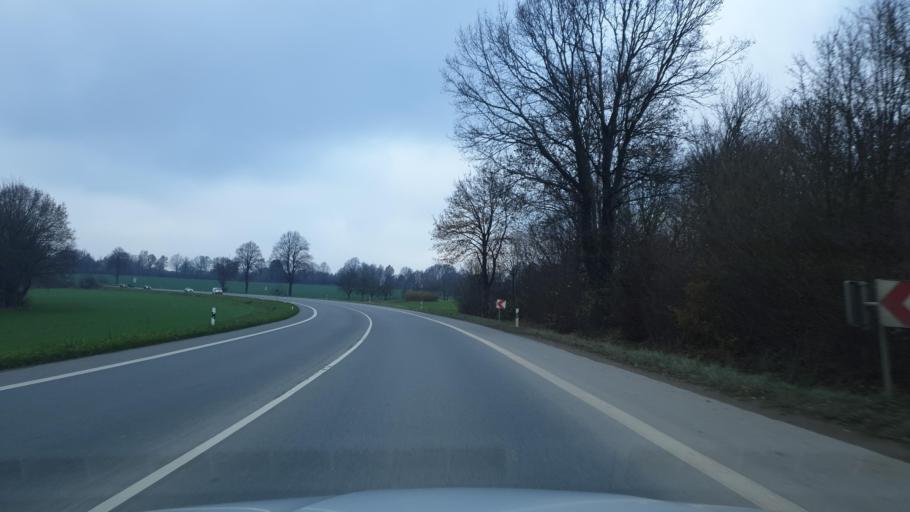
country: DE
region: North Rhine-Westphalia
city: Enger
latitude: 52.0972
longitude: 8.5841
